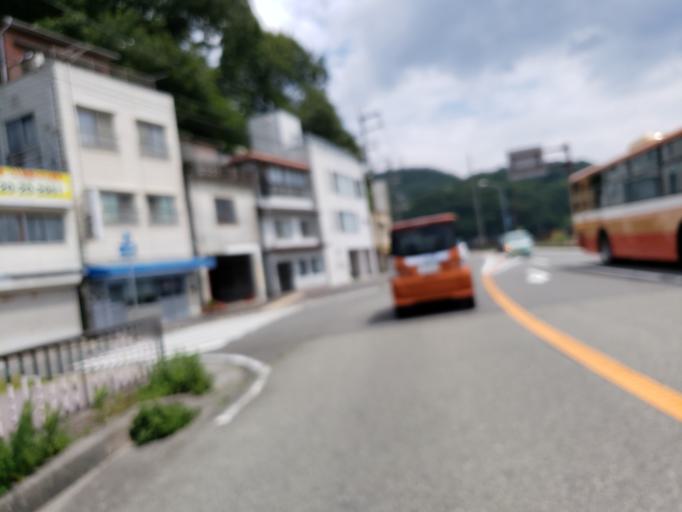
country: JP
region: Hyogo
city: Aioi
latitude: 34.8008
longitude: 134.4683
